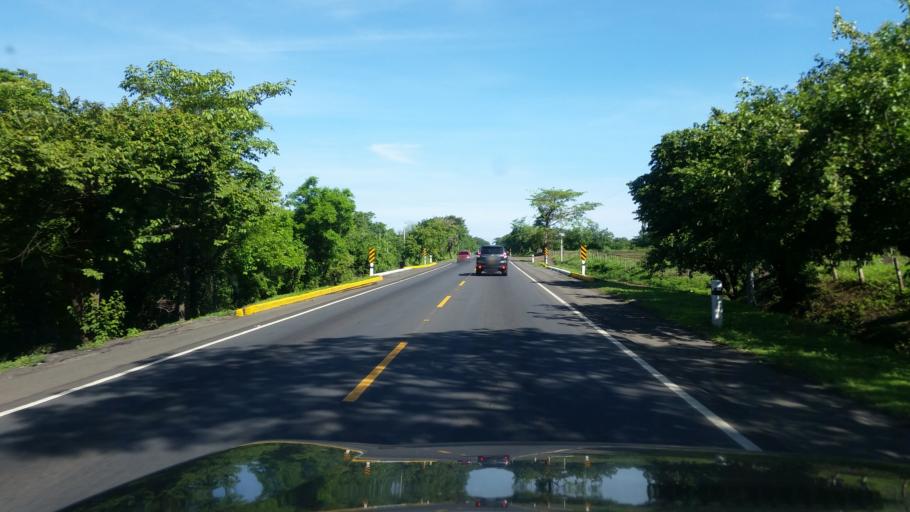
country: NI
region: Chinandega
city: Posoltega
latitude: 12.5594
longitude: -86.9536
